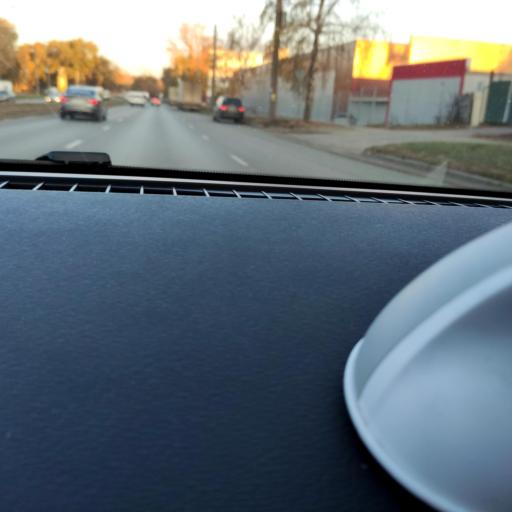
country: RU
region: Samara
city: Samara
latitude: 53.2019
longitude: 50.2331
